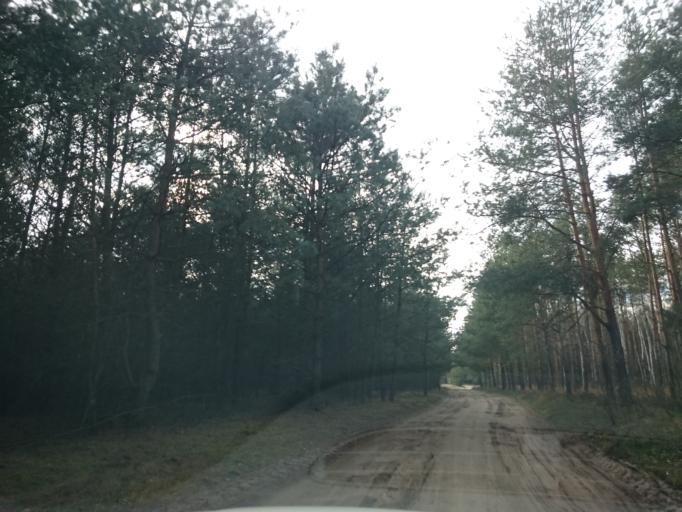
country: PL
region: Kujawsko-Pomorskie
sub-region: Powiat golubsko-dobrzynski
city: Ciechocin
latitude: 53.0499
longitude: 18.8614
